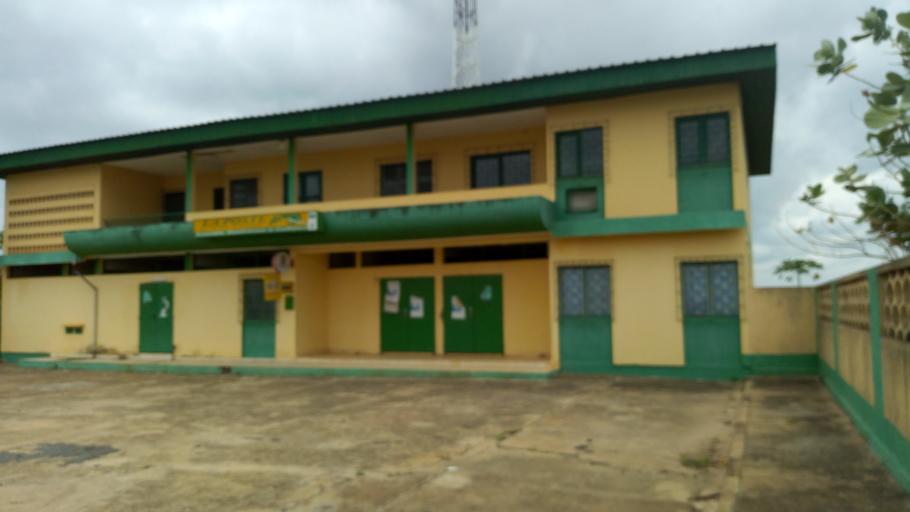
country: CI
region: Vallee du Bandama
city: Bouake
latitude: 7.6806
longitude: -5.0572
